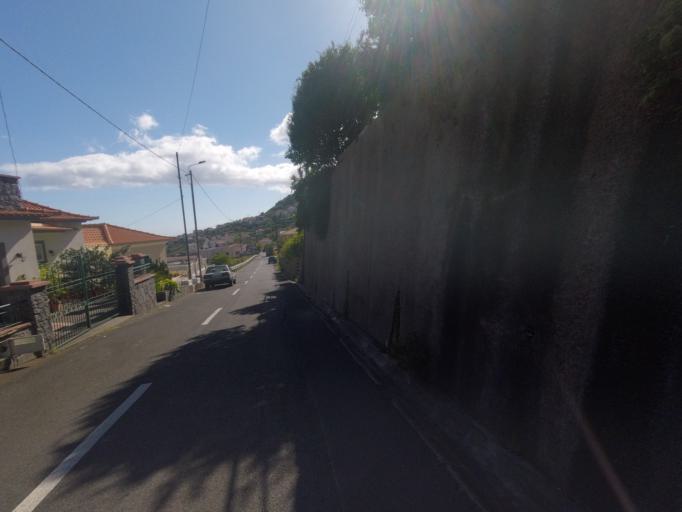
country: PT
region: Madeira
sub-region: Ribeira Brava
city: Campanario
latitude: 32.6758
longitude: -17.0276
